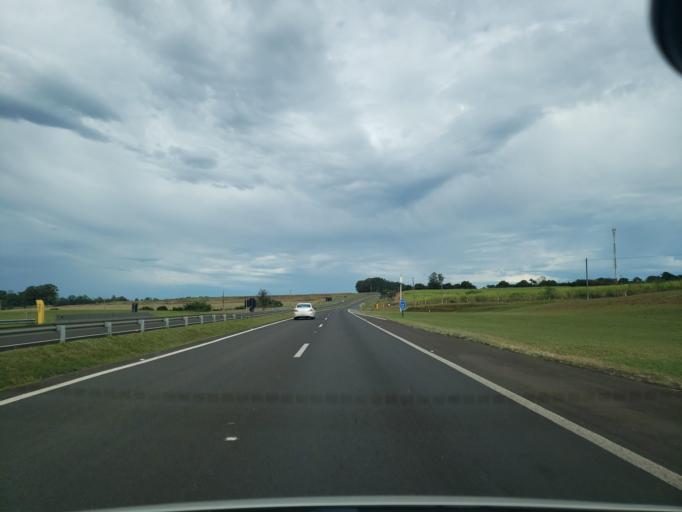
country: BR
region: Sao Paulo
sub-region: Dois Corregos
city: Dois Corregos
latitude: -22.2649
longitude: -48.3812
